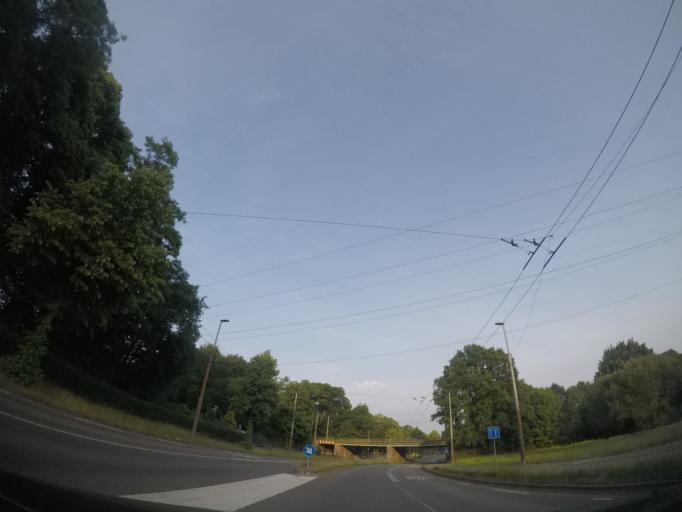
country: NL
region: Gelderland
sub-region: Gemeente Renkum
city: Oosterbeek
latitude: 51.9852
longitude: 5.8646
